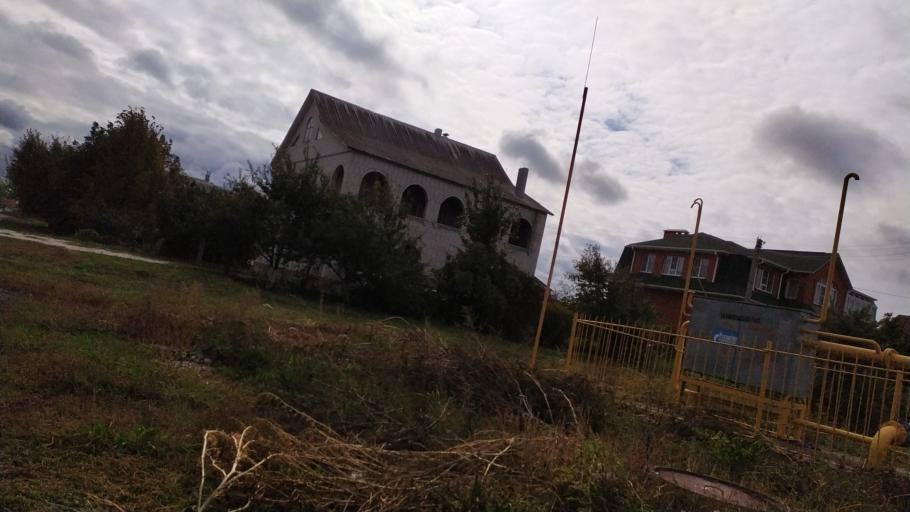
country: RU
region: Kursk
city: Kursk
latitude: 51.6441
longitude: 36.1538
